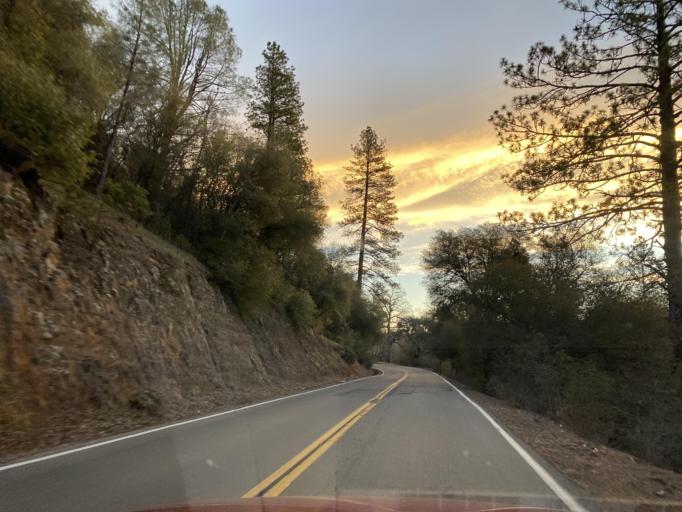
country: US
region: California
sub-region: Amador County
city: Plymouth
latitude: 38.4901
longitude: -120.7973
